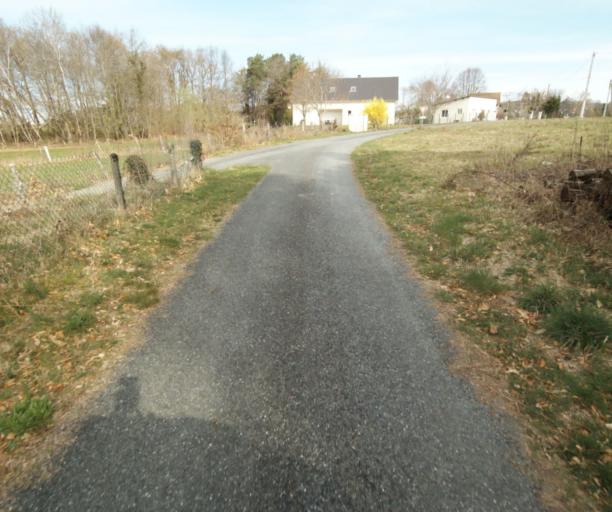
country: FR
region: Limousin
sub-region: Departement de la Correze
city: Correze
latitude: 45.4173
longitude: 1.8299
